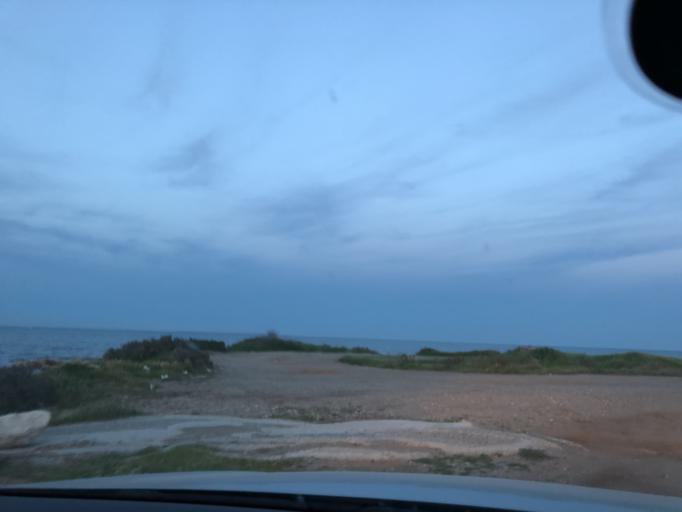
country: CY
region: Larnaka
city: Meneou
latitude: 34.8757
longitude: 33.6360
